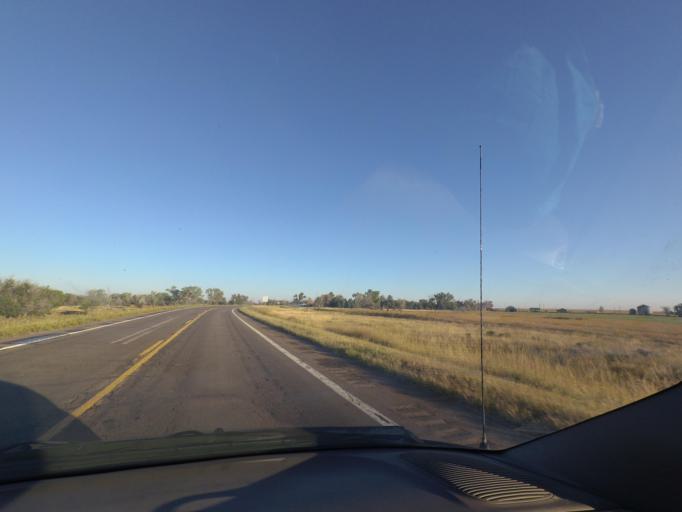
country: US
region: Colorado
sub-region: Yuma County
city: Yuma
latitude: 39.6595
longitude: -102.8491
